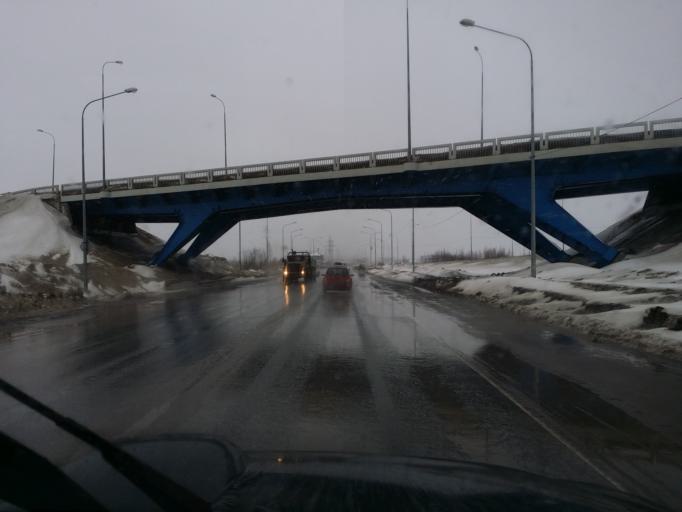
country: RU
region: Khanty-Mansiyskiy Avtonomnyy Okrug
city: Nizhnevartovsk
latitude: 60.9477
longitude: 76.6636
